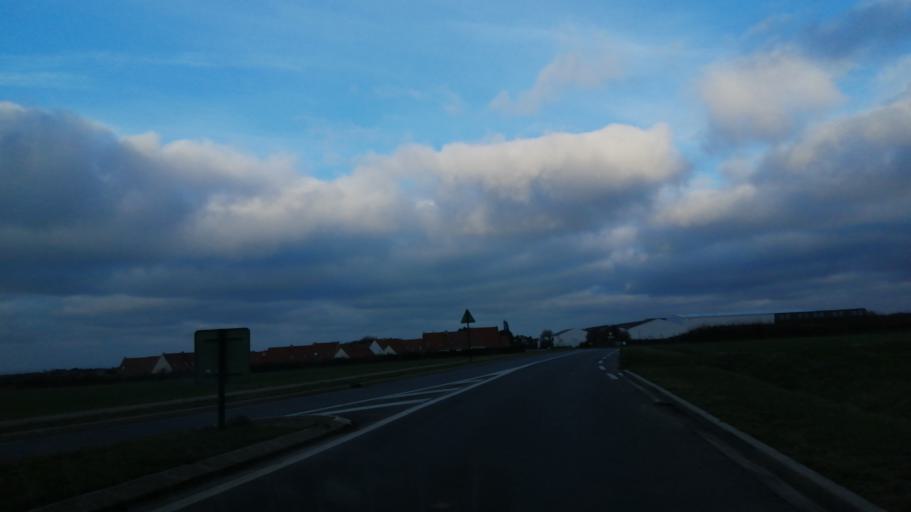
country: FR
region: Nord-Pas-de-Calais
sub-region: Departement du Pas-de-Calais
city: Ambleteuse
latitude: 50.8473
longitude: 1.6069
